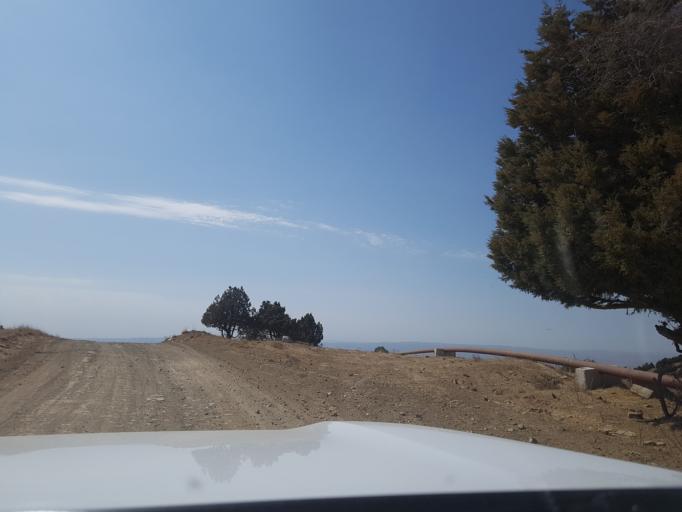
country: TM
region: Ahal
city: Baharly
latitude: 38.3191
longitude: 56.9547
